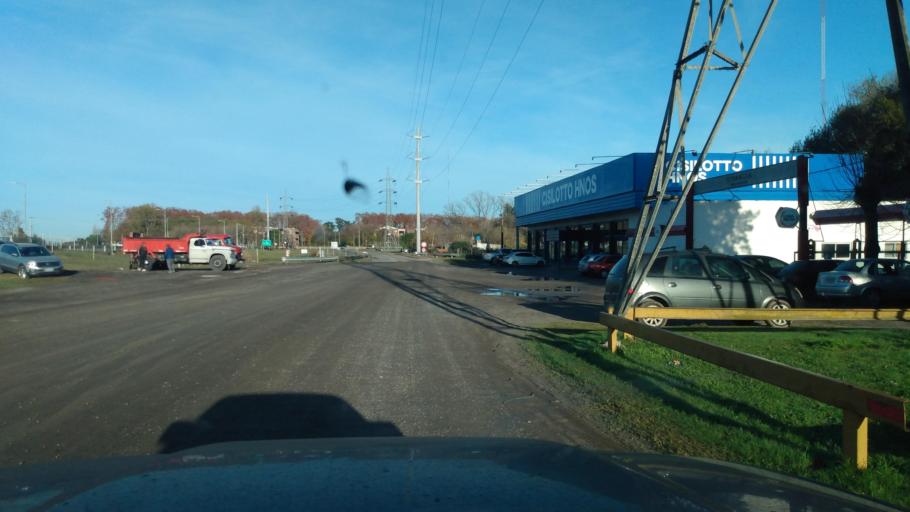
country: AR
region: Buenos Aires
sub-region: Partido de Lujan
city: Lujan
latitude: -34.5761
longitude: -59.0822
